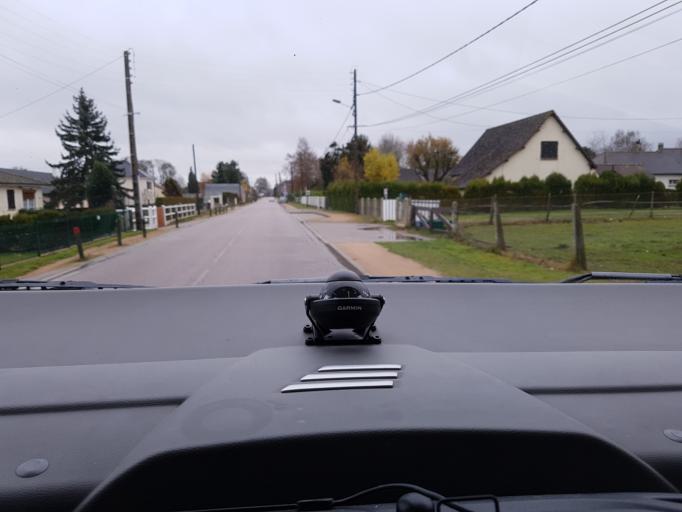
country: FR
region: Haute-Normandie
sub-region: Departement de l'Eure
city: Pont-Saint-Pierre
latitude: 49.3165
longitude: 1.3030
